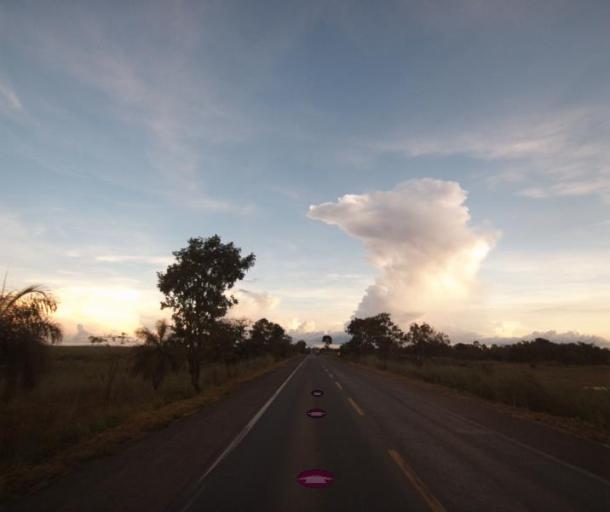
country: BR
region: Goias
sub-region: Uruacu
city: Uruacu
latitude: -14.4367
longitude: -49.1568
